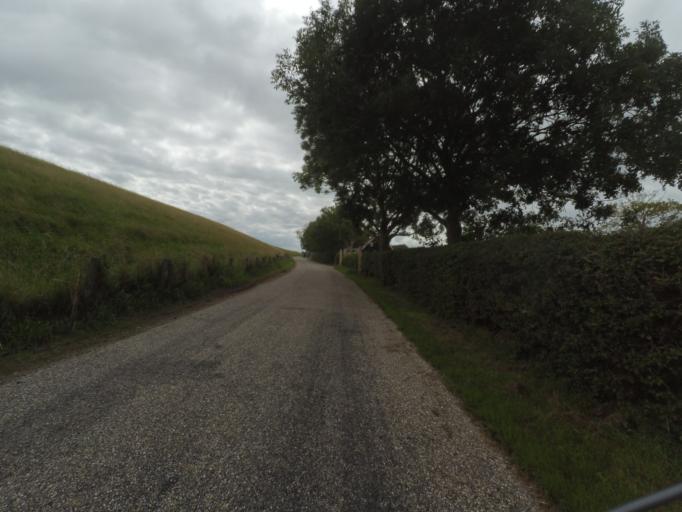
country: NL
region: Friesland
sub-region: Gemeente Dongeradeel
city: Anjum
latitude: 53.3580
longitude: 6.1473
